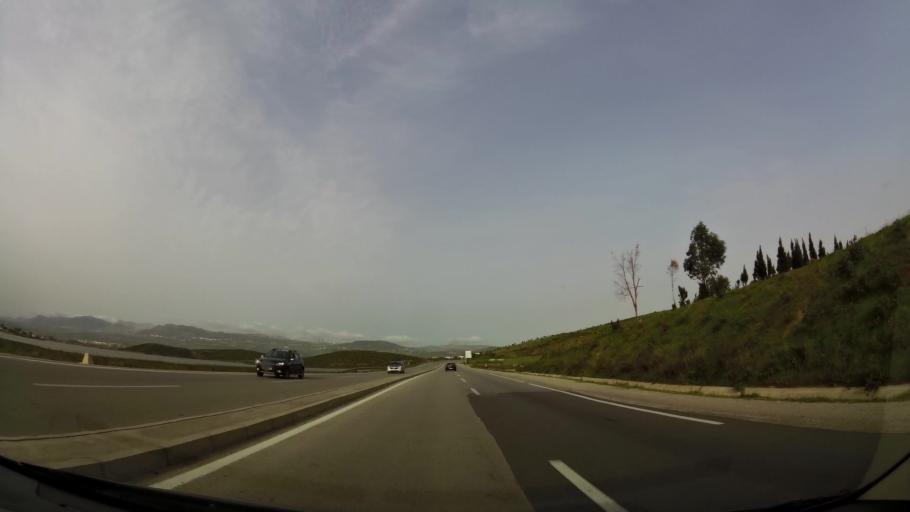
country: MA
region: Tanger-Tetouan
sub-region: Tetouan
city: Saddina
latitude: 35.5616
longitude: -5.4966
